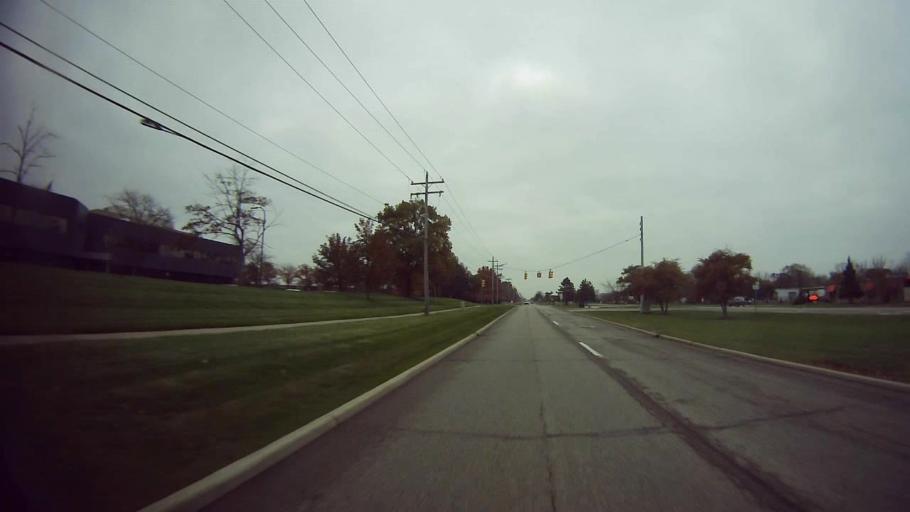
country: US
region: Michigan
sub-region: Oakland County
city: Clawson
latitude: 42.5415
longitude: -83.1201
